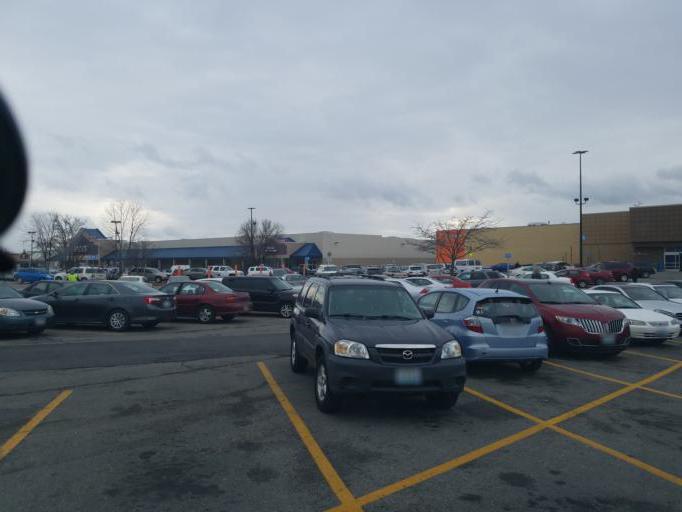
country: US
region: Missouri
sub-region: Boone County
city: Columbia
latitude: 38.9546
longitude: -92.2952
